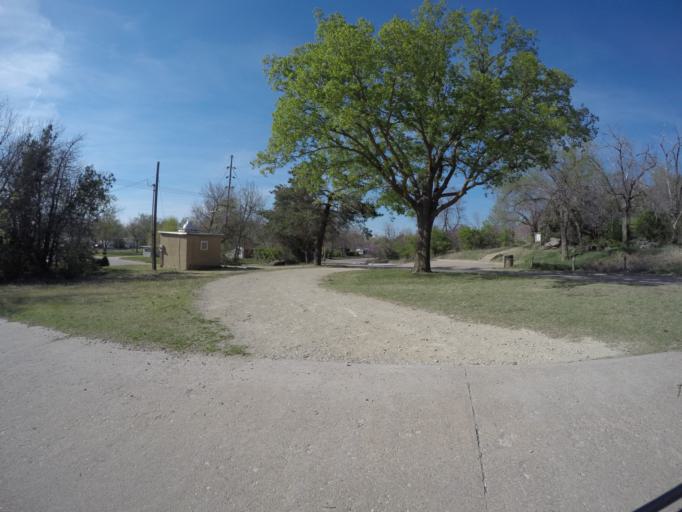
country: US
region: Kansas
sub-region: Saline County
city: Salina
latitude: 38.8340
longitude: -97.5893
